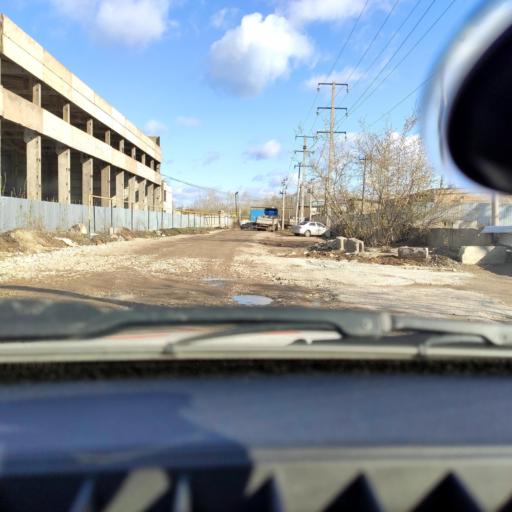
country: RU
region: Bashkortostan
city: Ufa
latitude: 54.7455
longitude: 55.9292
